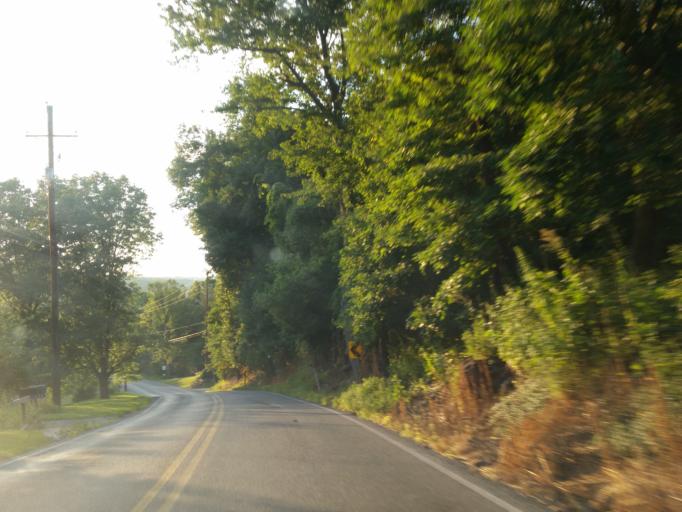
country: US
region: Pennsylvania
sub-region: Lancaster County
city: Adamstown
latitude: 40.2480
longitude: -76.0265
